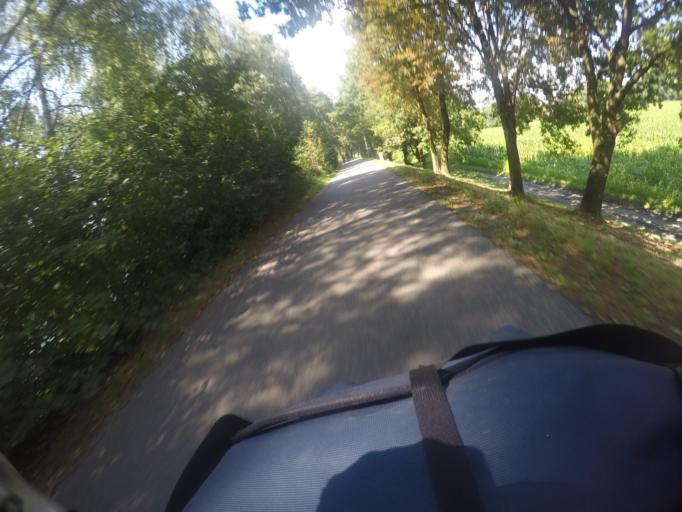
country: CH
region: Saint Gallen
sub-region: Wahlkreis Rheintal
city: Diepoldsau
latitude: 47.3901
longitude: 9.6761
